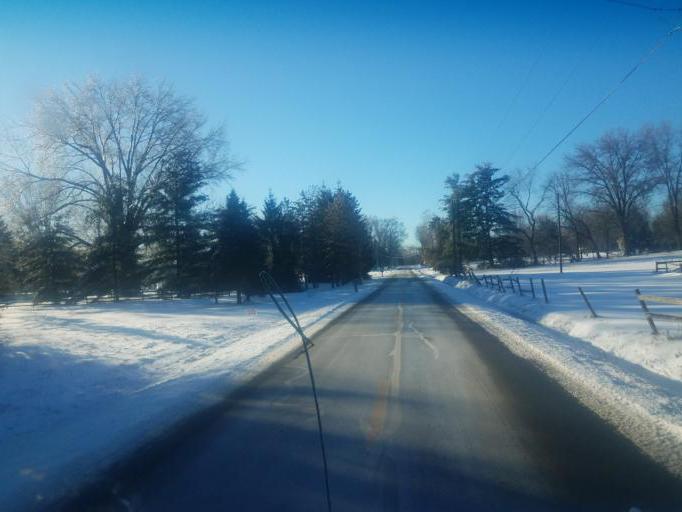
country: US
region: Ohio
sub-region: Delaware County
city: Sunbury
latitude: 40.2133
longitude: -82.9133
